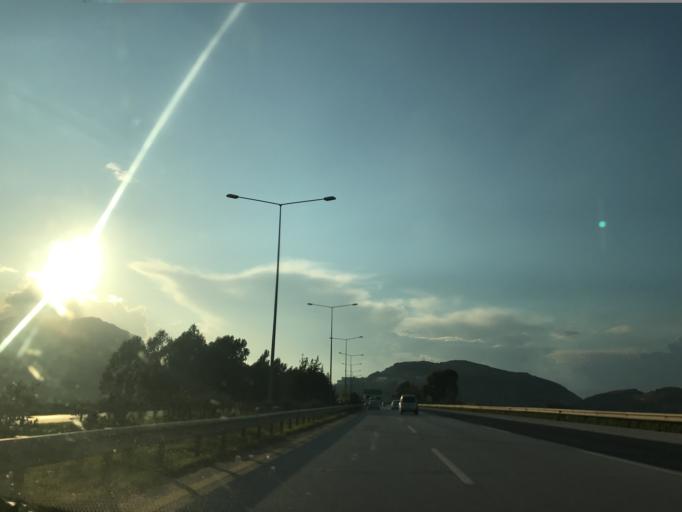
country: TR
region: Adana
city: Ceyhan
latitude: 36.9870
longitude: 35.7608
